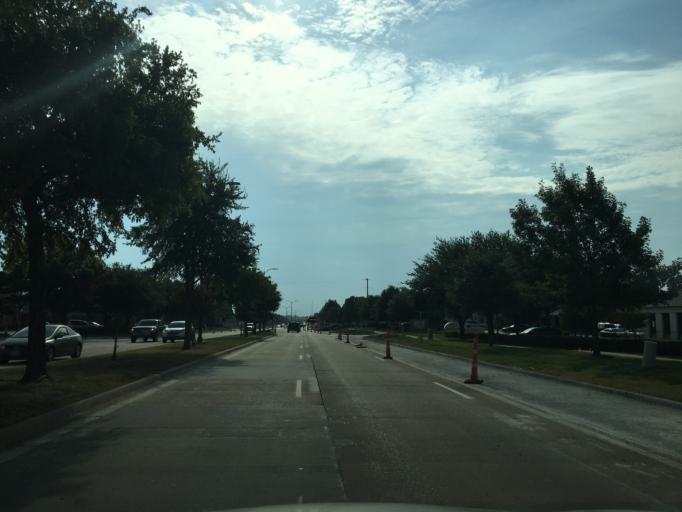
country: US
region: Texas
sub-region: Collin County
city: McKinney
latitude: 33.1988
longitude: -96.6514
